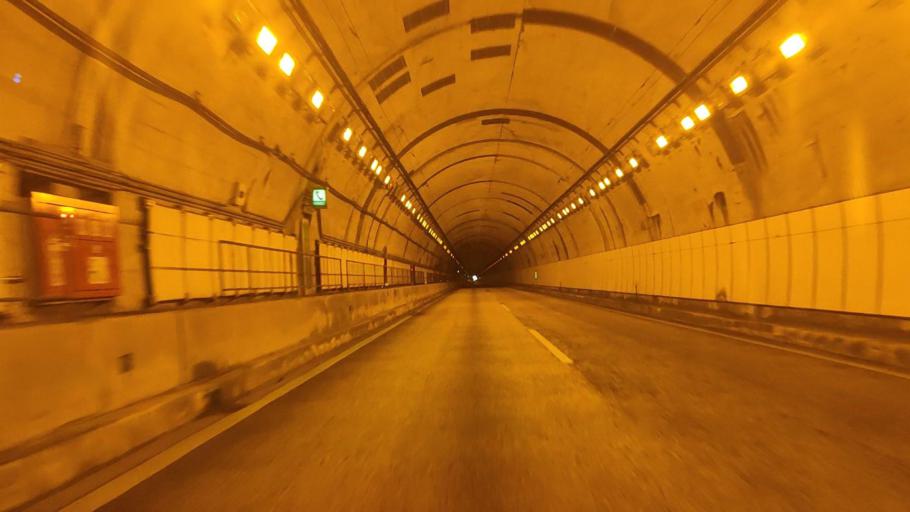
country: JP
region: Miyazaki
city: Miyakonojo
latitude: 31.8236
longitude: 131.2331
